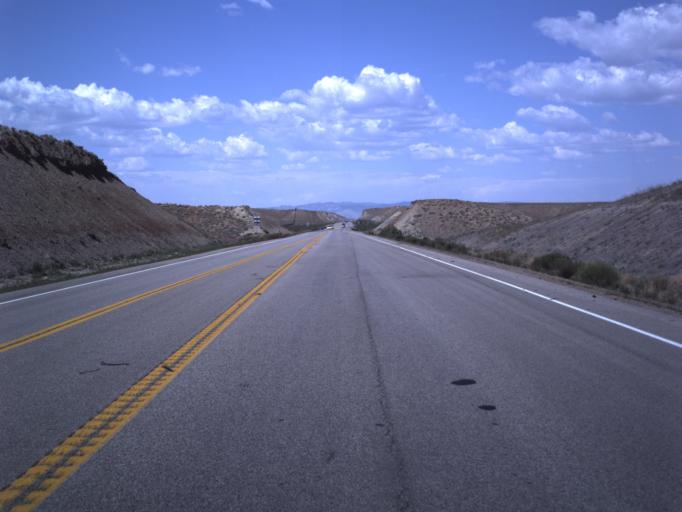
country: US
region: Utah
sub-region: Emery County
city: Huntington
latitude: 39.4354
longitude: -110.8669
